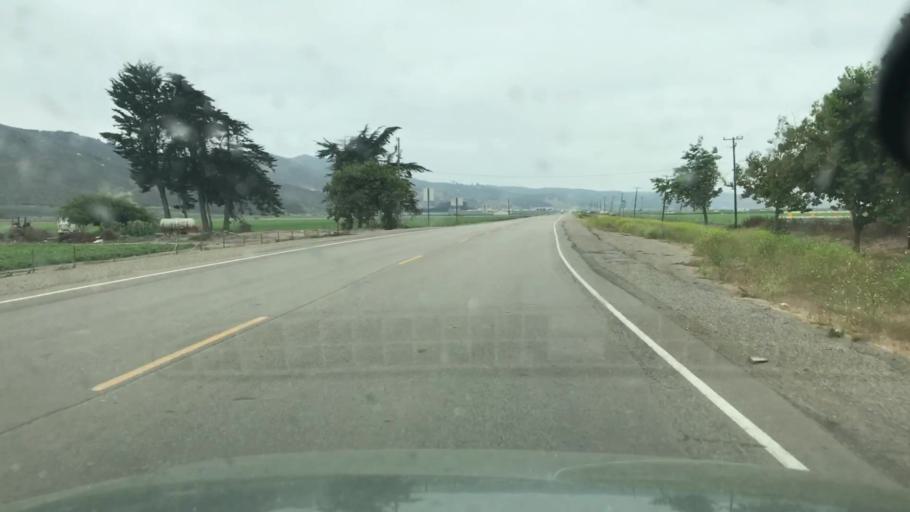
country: US
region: California
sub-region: Santa Barbara County
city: Lompoc
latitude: 34.6392
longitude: -120.4751
